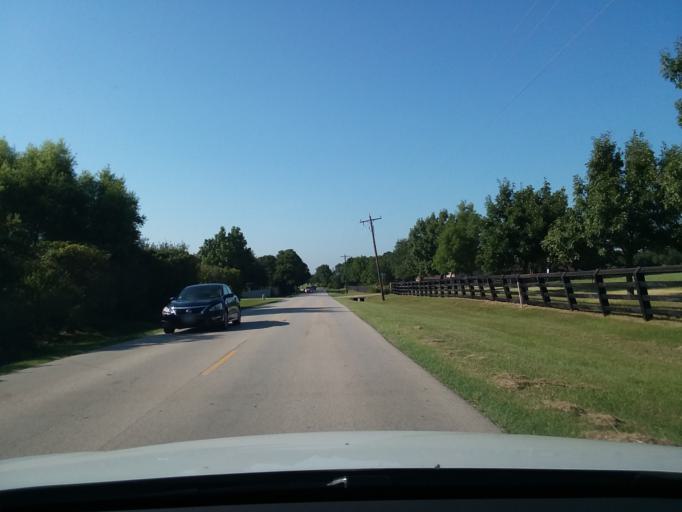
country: US
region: Texas
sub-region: Denton County
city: Bartonville
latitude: 33.0619
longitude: -97.1316
